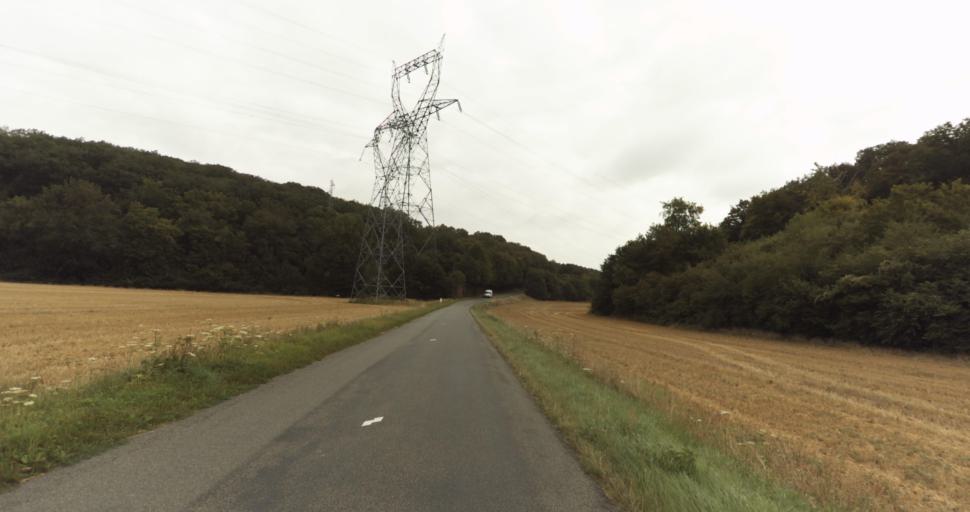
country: FR
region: Haute-Normandie
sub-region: Departement de l'Eure
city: Croth
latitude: 48.8784
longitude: 1.3718
